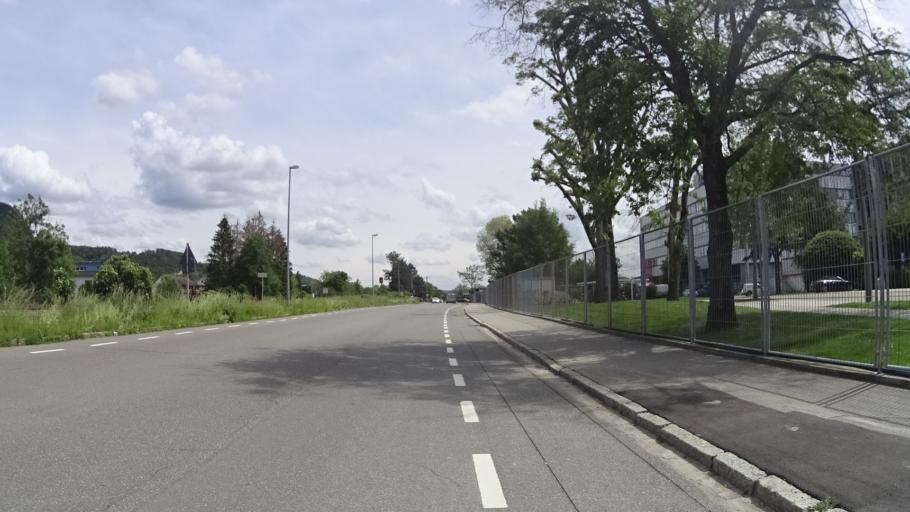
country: DE
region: Baden-Wuerttemberg
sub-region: Freiburg Region
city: Grenzach-Wyhlen
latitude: 47.5497
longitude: 7.6666
